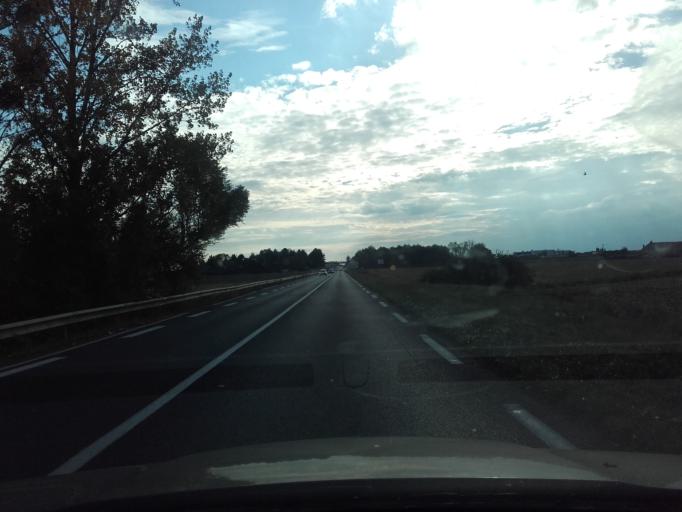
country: FR
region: Centre
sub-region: Departement d'Indre-et-Loire
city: Parcay-Meslay
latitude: 47.4577
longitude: 0.7378
